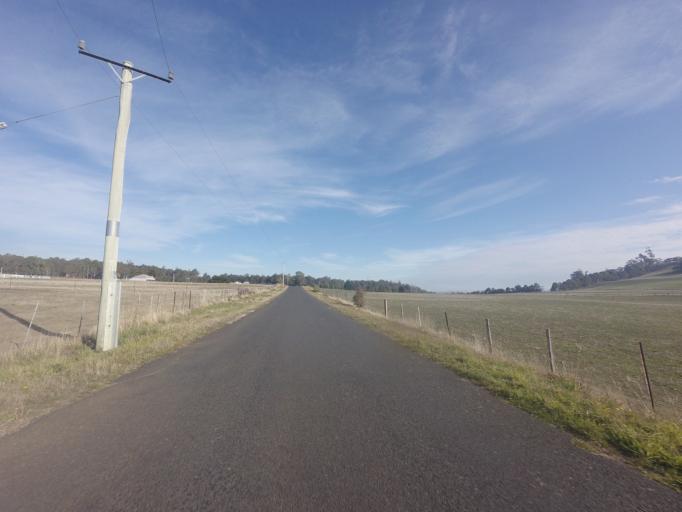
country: AU
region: Tasmania
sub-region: Sorell
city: Sorell
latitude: -42.4780
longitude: 147.4574
